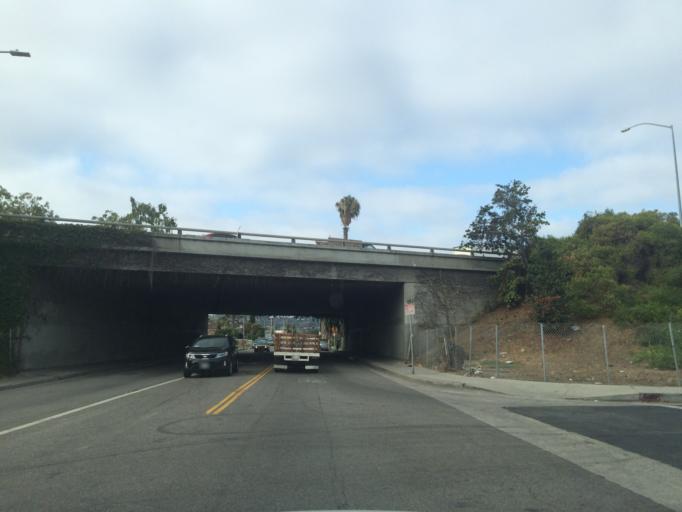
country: US
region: California
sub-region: Los Angeles County
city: View Park-Windsor Hills
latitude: 34.0346
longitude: -118.3555
